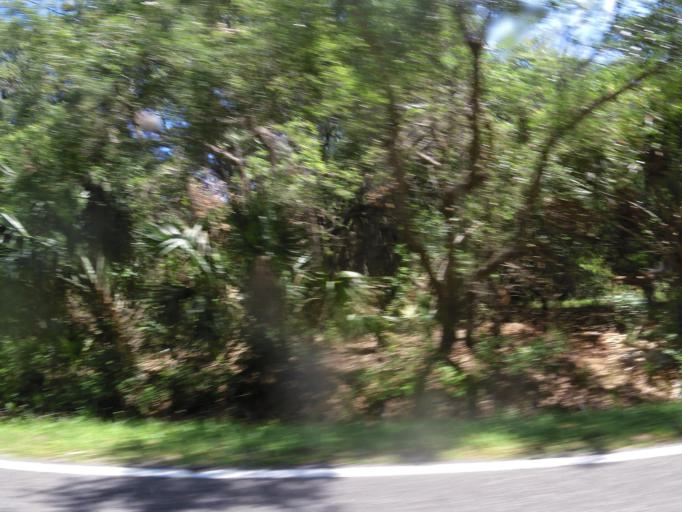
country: US
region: Florida
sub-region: Duval County
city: Atlantic Beach
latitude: 30.4535
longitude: -81.4661
